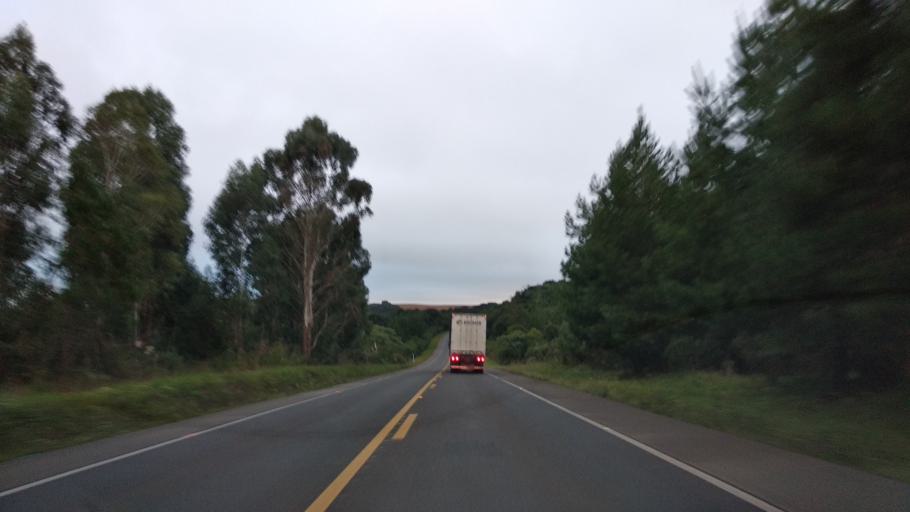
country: BR
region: Santa Catarina
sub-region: Campos Novos
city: Campos Novos
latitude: -27.3783
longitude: -51.0944
